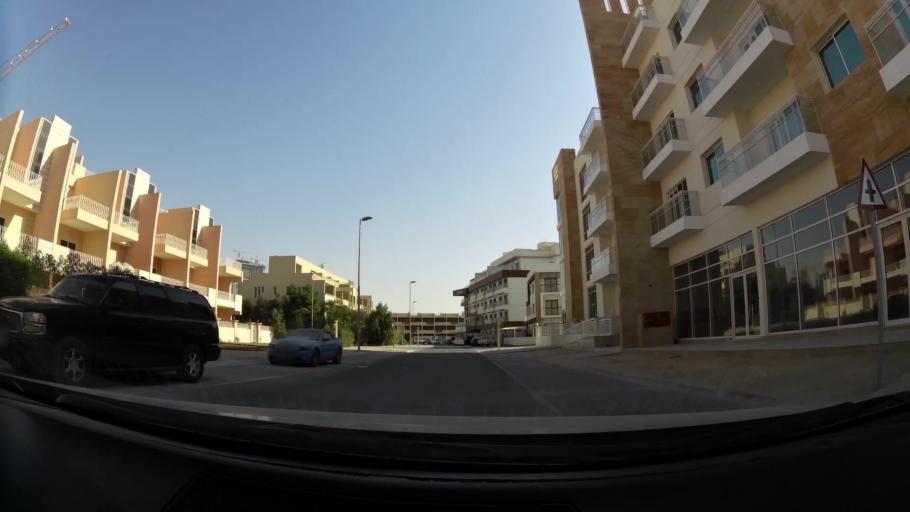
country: AE
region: Dubai
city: Dubai
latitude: 25.0611
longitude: 55.1993
